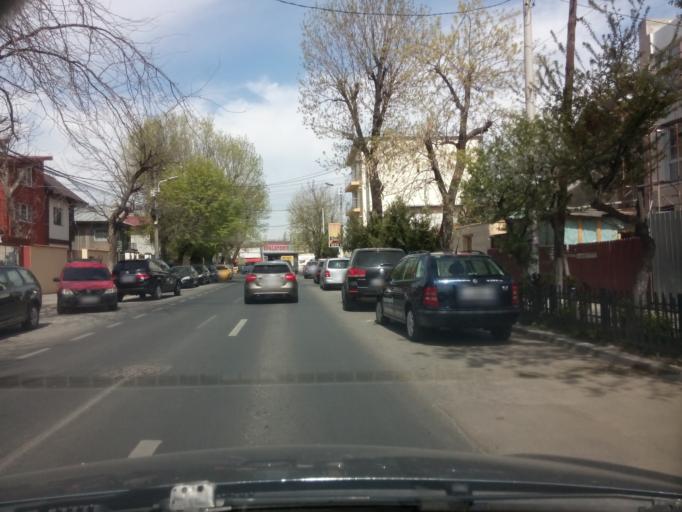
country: RO
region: Bucuresti
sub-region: Municipiul Bucuresti
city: Bucharest
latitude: 44.4646
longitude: 26.1174
